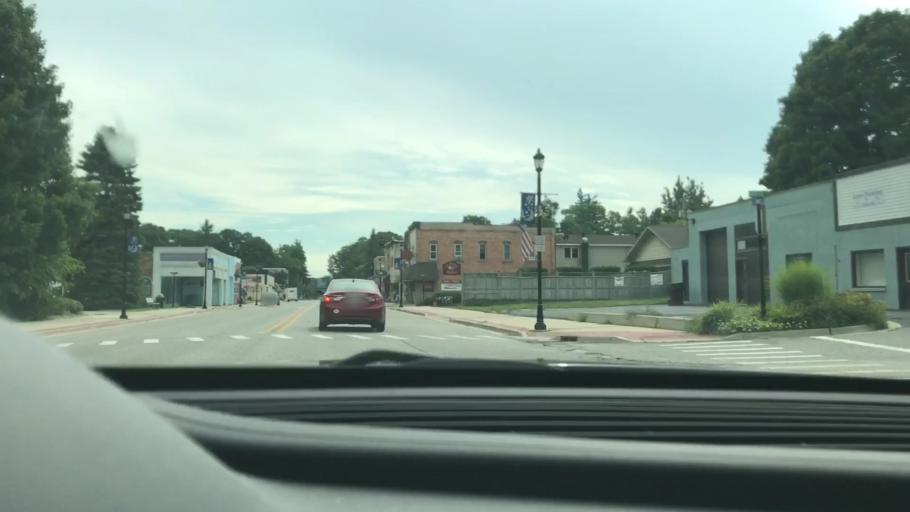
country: US
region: Michigan
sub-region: Antrim County
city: Bellaire
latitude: 45.0716
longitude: -85.2642
